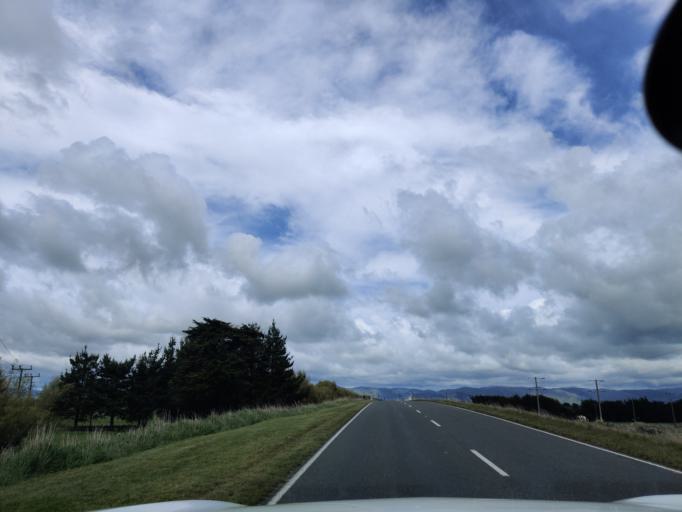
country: NZ
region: Manawatu-Wanganui
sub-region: Palmerston North City
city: Palmerston North
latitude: -40.3661
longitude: 175.5523
